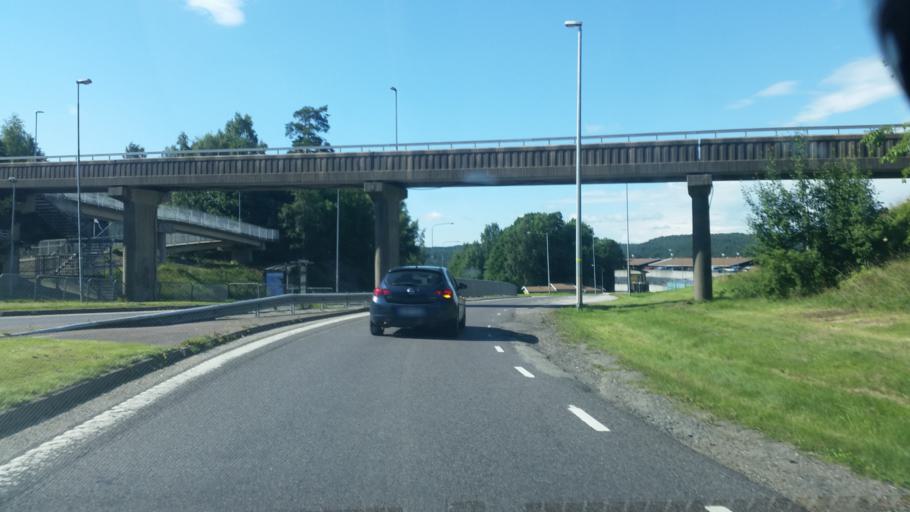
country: SE
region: Vaestra Goetaland
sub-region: Partille Kommun
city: Partille
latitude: 57.7303
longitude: 12.1106
